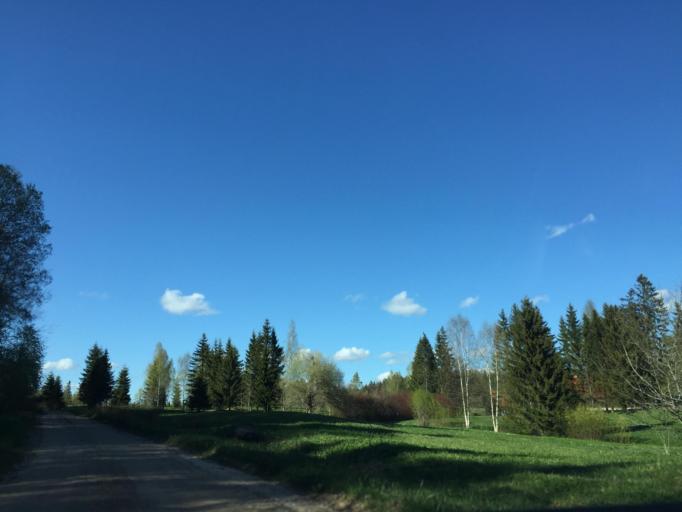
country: LV
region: Madonas Rajons
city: Madona
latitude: 56.8662
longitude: 25.9711
